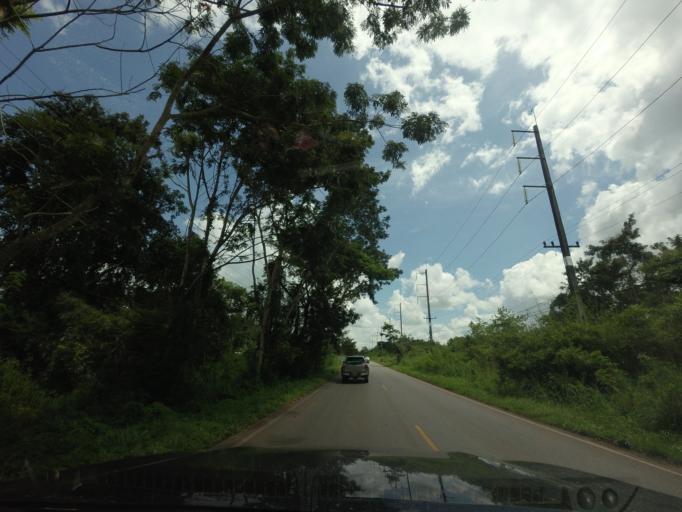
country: TH
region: Nong Khai
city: Sa Khrai
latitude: 17.5742
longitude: 102.6468
